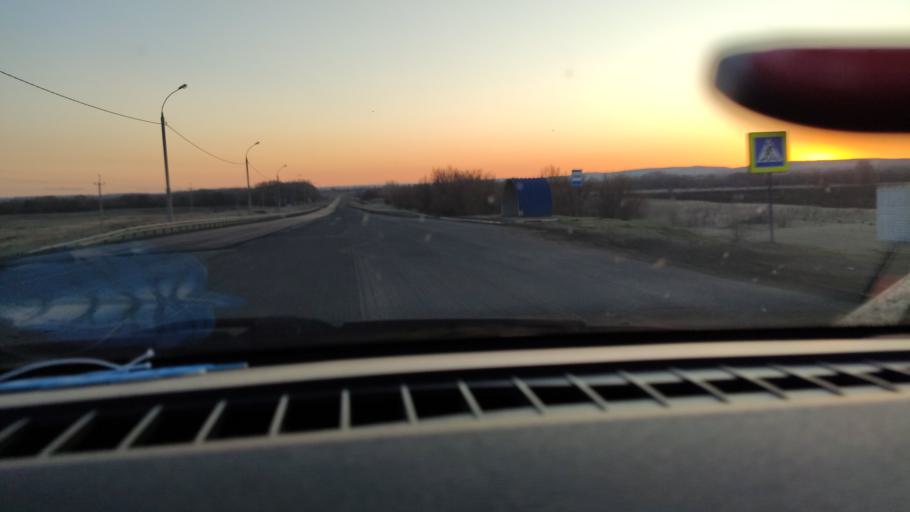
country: RU
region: Saratov
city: Yelshanka
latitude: 51.8173
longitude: 46.2128
